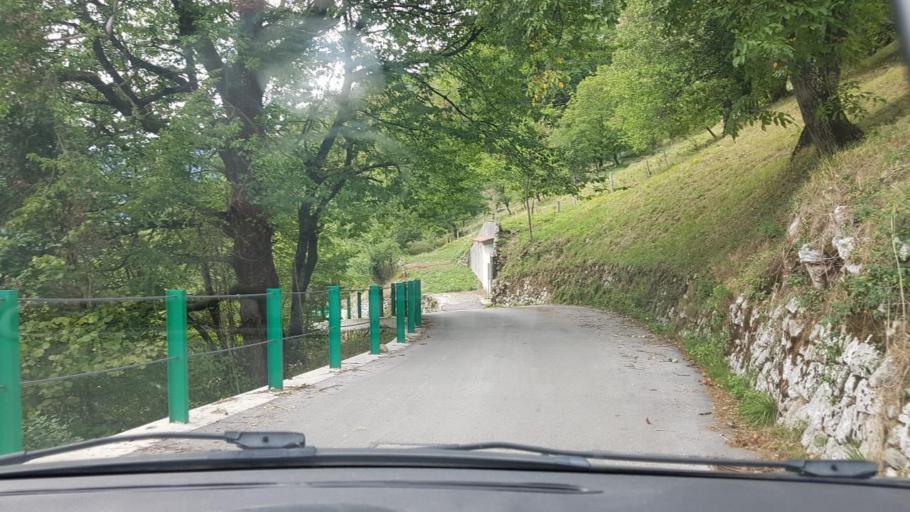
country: SI
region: Tolmin
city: Tolmin
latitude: 46.2019
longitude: 13.7479
